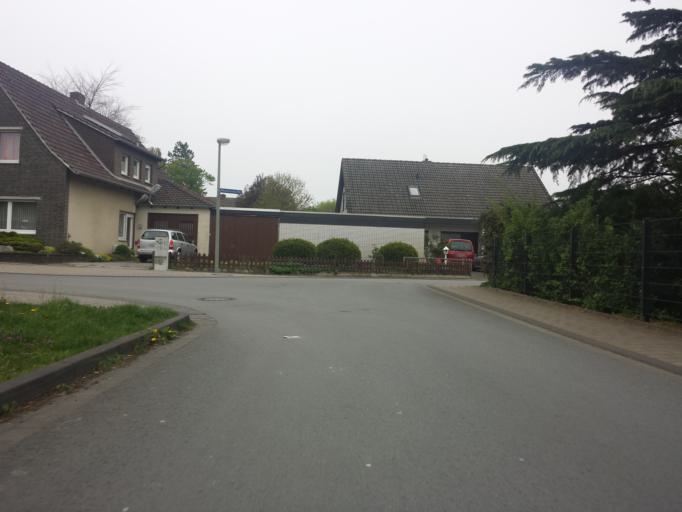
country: DE
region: North Rhine-Westphalia
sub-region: Regierungsbezirk Detmold
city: Guetersloh
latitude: 51.8914
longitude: 8.3784
